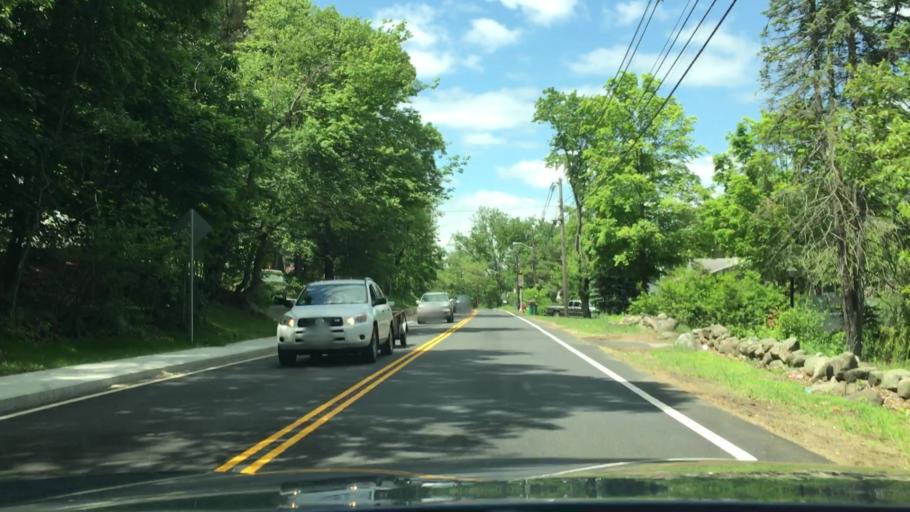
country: US
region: Massachusetts
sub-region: Middlesex County
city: Billerica
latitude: 42.5725
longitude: -71.2710
